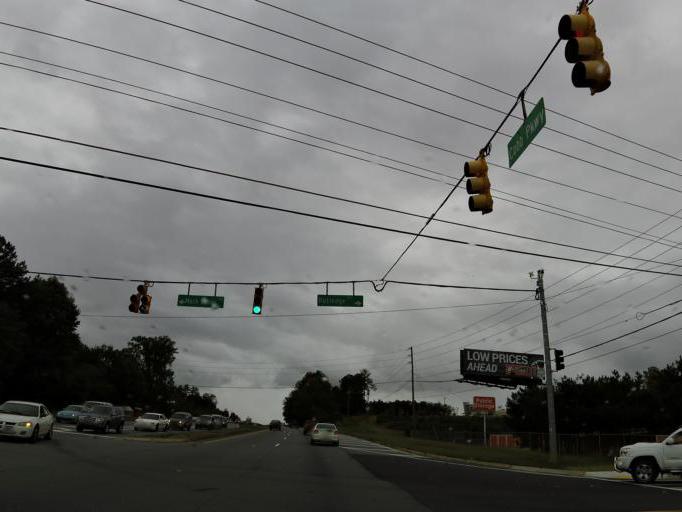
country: US
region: Georgia
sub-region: Cobb County
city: Kennesaw
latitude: 34.0269
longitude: -84.6375
